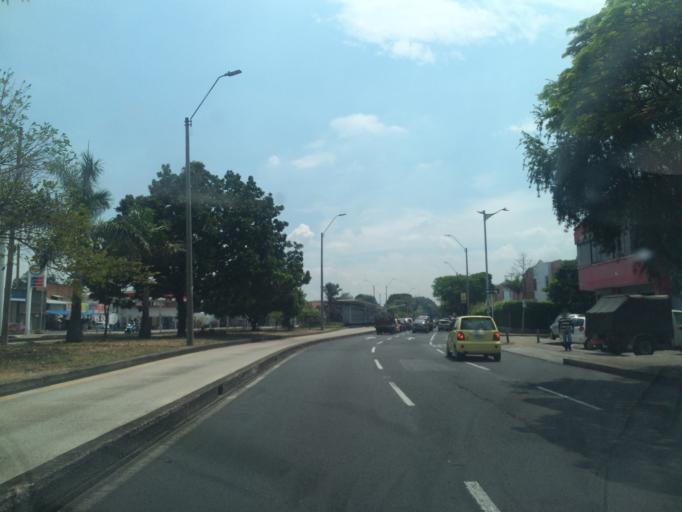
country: CO
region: Valle del Cauca
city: Cali
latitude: 3.4775
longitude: -76.5030
